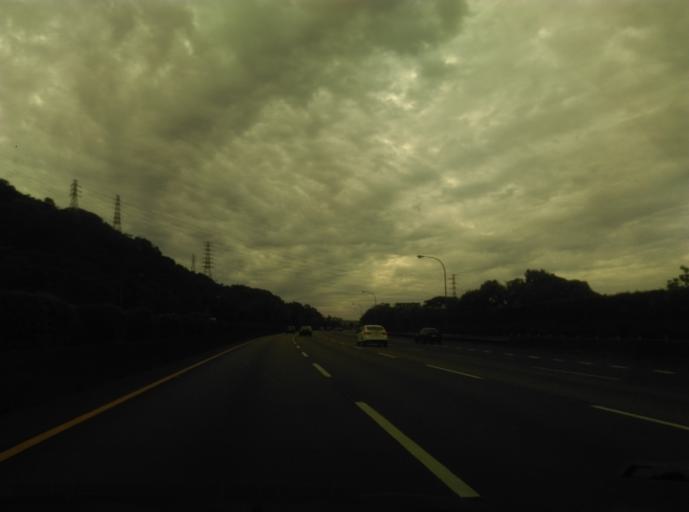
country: TW
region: Taiwan
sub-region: Taoyuan
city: Taoyuan
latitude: 24.9367
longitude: 121.3568
